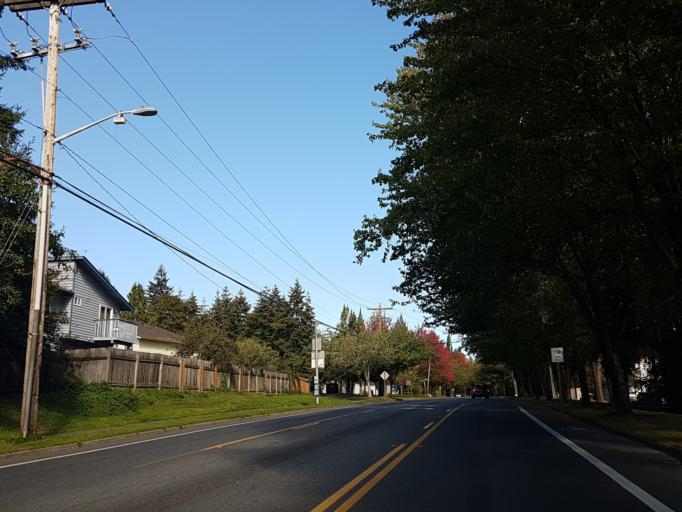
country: US
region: Washington
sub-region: King County
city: Lake Forest Park
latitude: 47.7667
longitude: -122.2642
